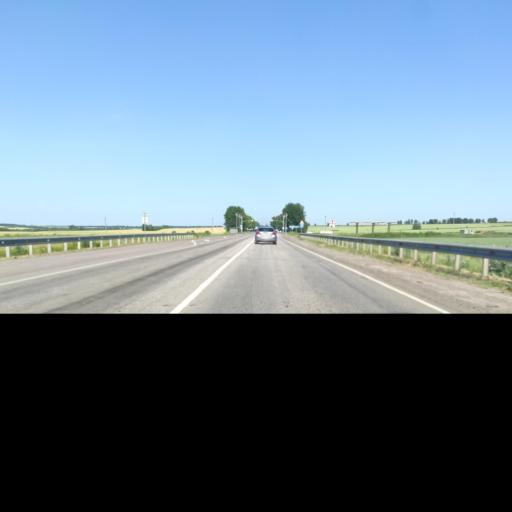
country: RU
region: Voronezj
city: Verkhnyaya Khava
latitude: 51.6879
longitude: 39.9264
